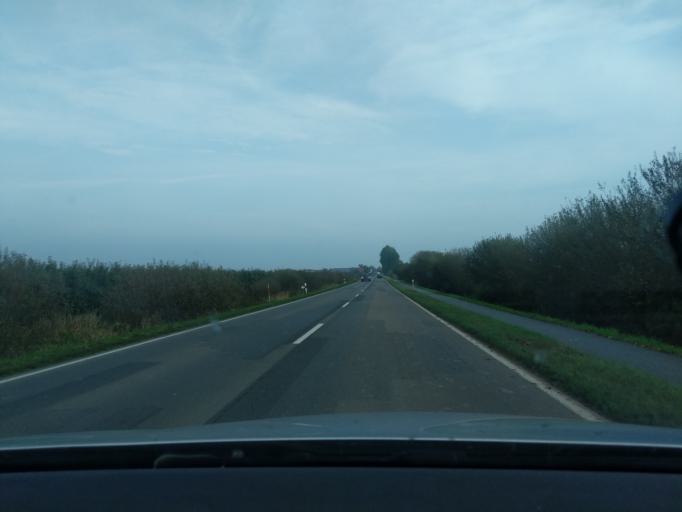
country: DE
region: Lower Saxony
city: Guderhandviertel
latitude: 53.5446
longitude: 9.5972
